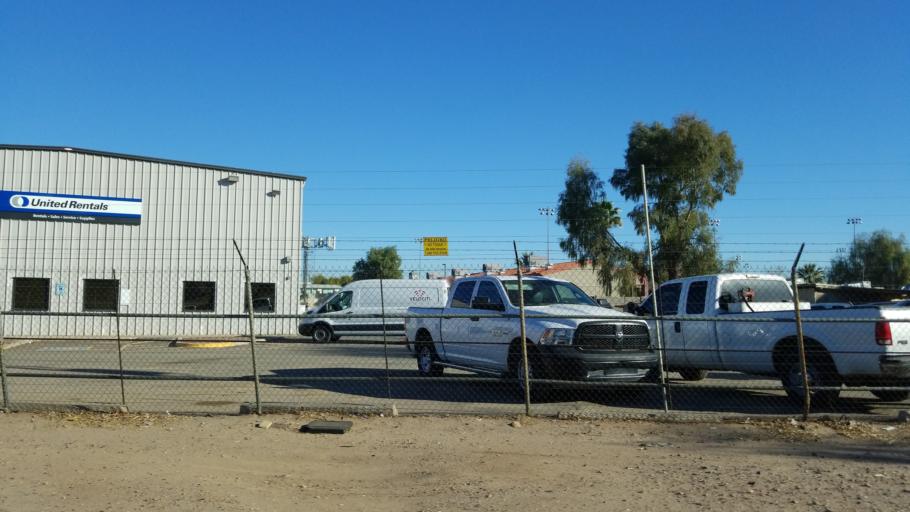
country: US
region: Arizona
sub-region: Maricopa County
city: Phoenix
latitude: 33.4296
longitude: -112.1043
